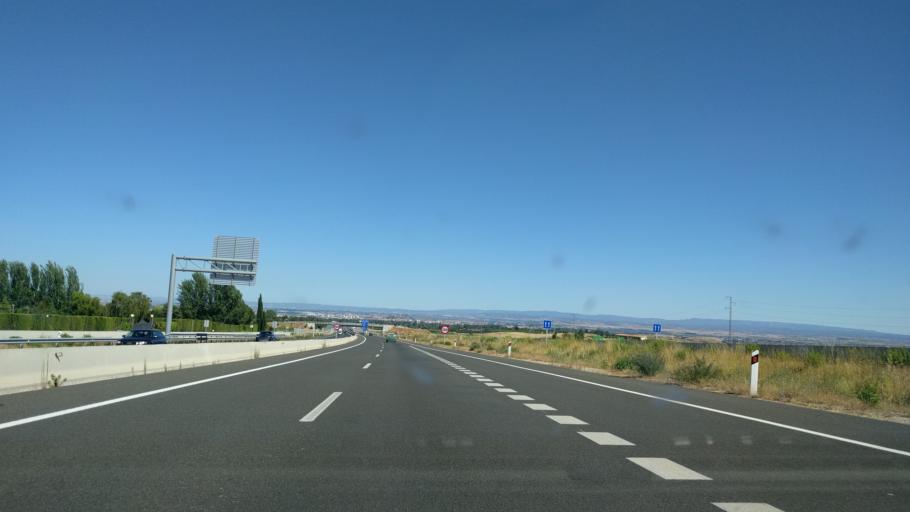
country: ES
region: Catalonia
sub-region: Provincia de Lleida
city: Alpicat
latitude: 41.6575
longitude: 0.5354
